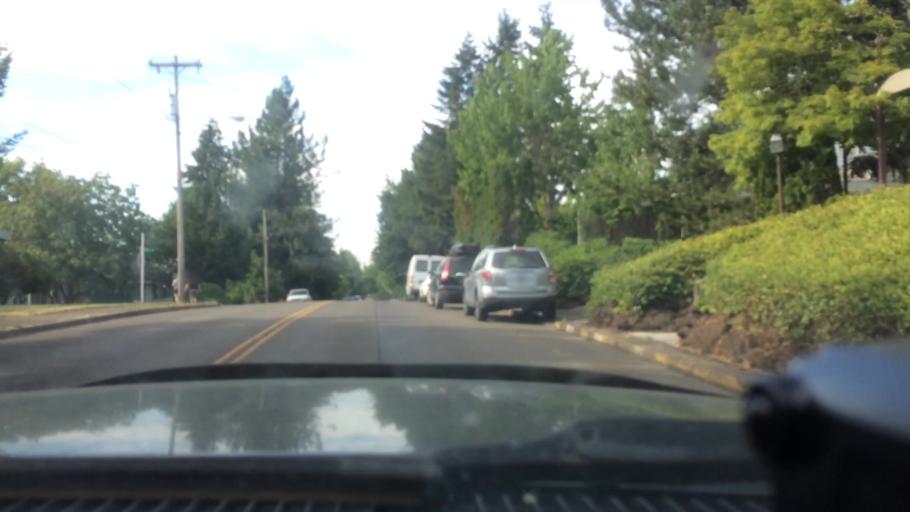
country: US
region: Oregon
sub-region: Lane County
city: Eugene
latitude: 44.0316
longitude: -123.1012
